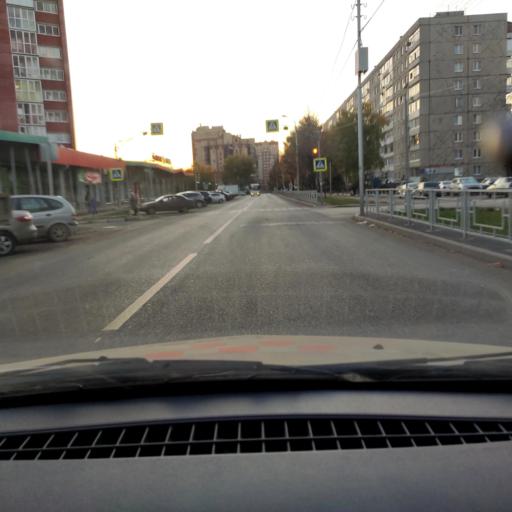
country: RU
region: Bashkortostan
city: Ufa
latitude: 54.7810
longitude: 56.1286
